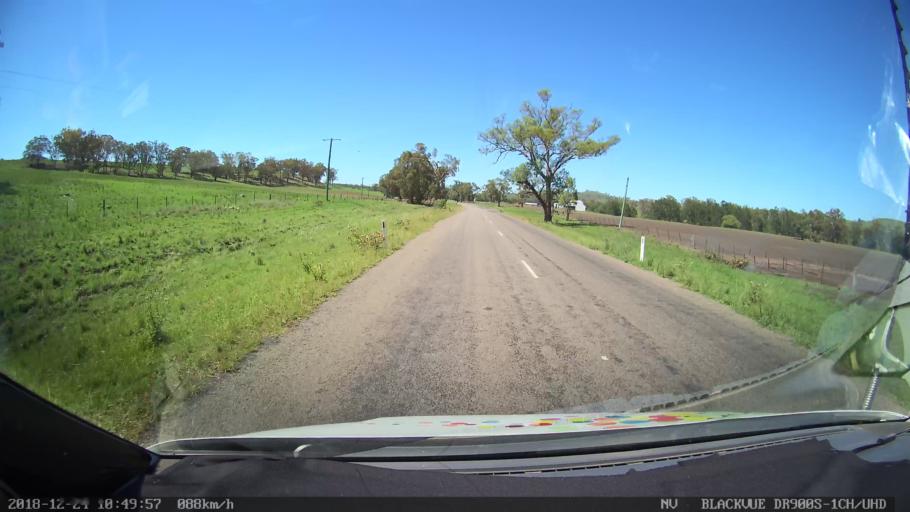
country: AU
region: New South Wales
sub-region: Upper Hunter Shire
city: Merriwa
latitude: -31.9540
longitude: 150.4252
